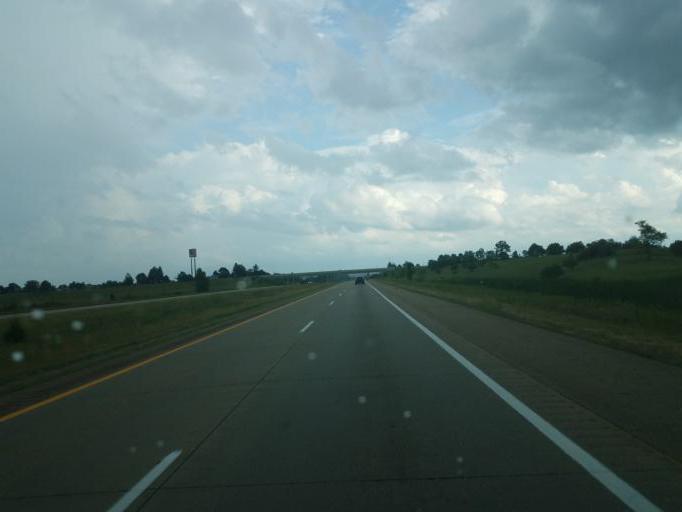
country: US
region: Michigan
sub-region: Calhoun County
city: Marshall
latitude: 42.2730
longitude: -84.9924
